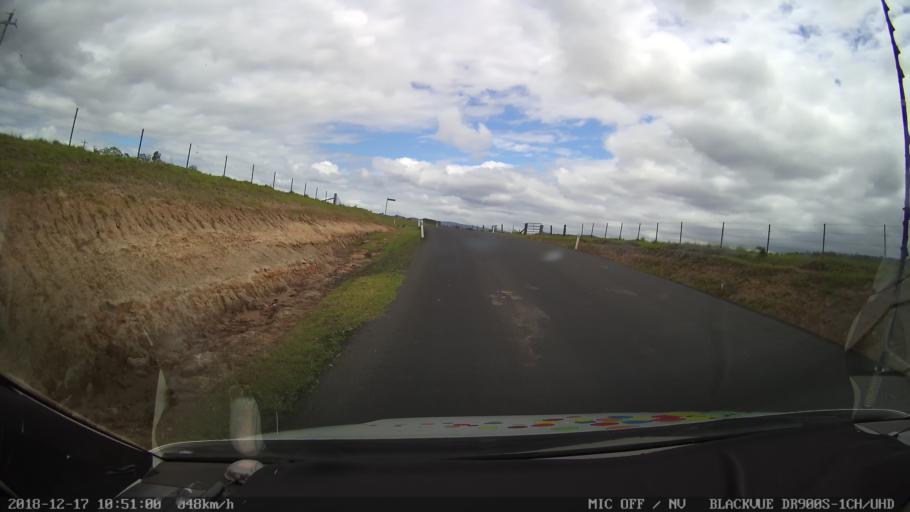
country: AU
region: New South Wales
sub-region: Tenterfield Municipality
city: Carrolls Creek
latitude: -28.8550
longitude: 152.5693
